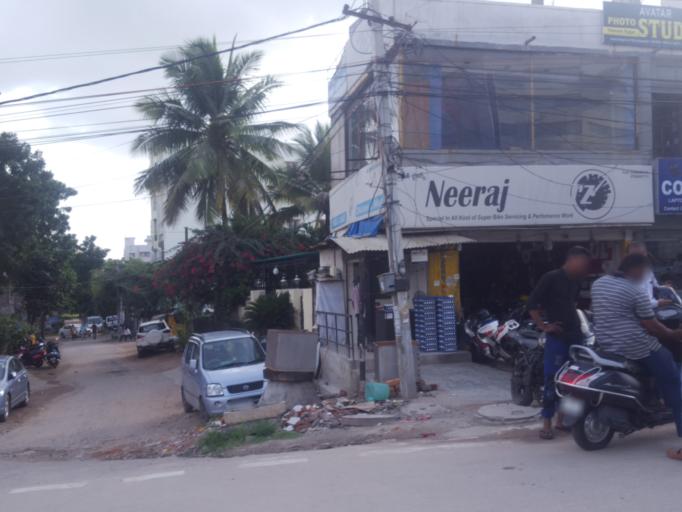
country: IN
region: Telangana
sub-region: Rangareddi
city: Kukatpalli
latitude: 17.4357
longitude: 78.3671
